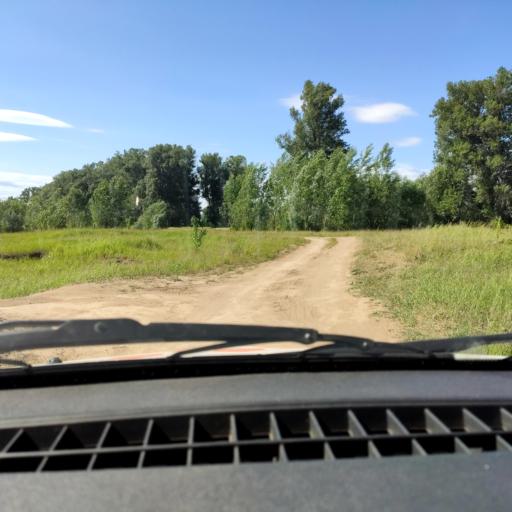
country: RU
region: Bashkortostan
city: Iglino
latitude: 54.8015
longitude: 56.2224
